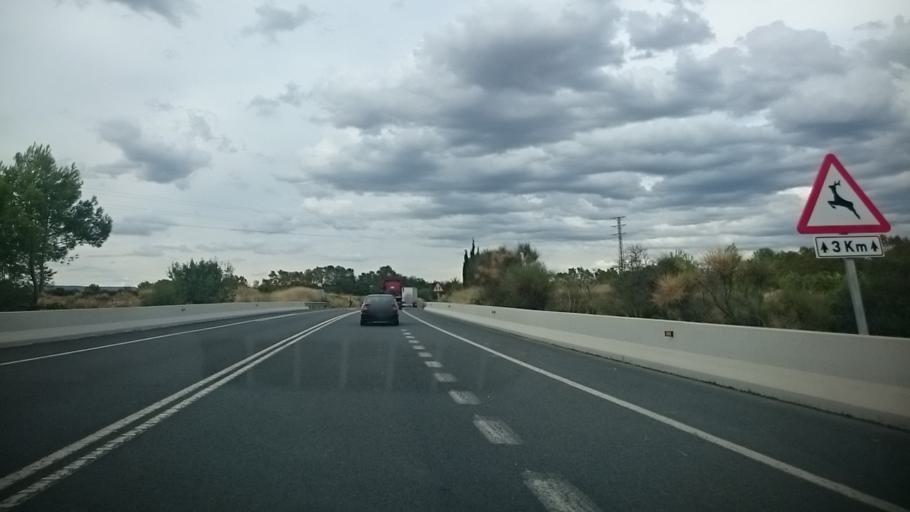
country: ES
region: Catalonia
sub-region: Provincia de Barcelona
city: Castellet
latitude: 41.3153
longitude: 1.6407
